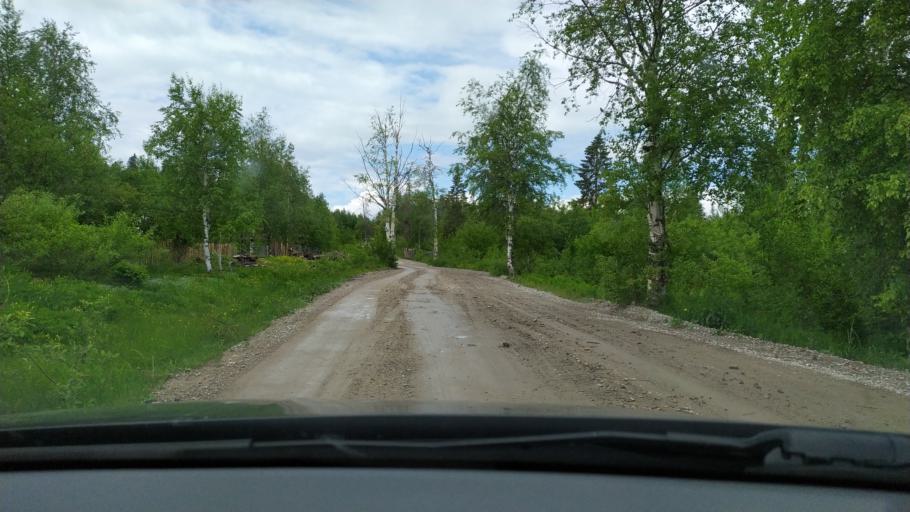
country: RU
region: Perm
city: Gremyachinsk
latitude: 58.5104
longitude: 57.8229
